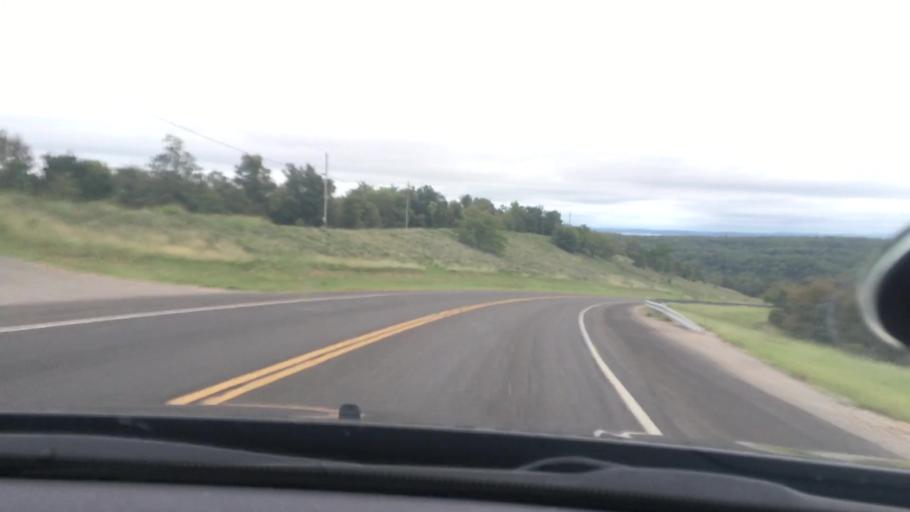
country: US
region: Oklahoma
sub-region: Sequoyah County
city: Vian
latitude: 35.5499
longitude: -94.9701
